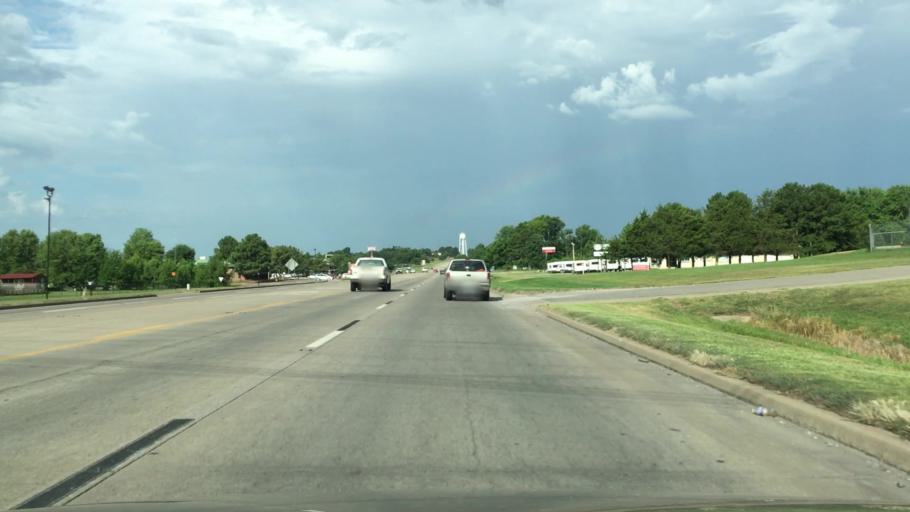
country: US
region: Oklahoma
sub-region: Cherokee County
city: Park Hill
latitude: 35.8554
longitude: -94.9855
